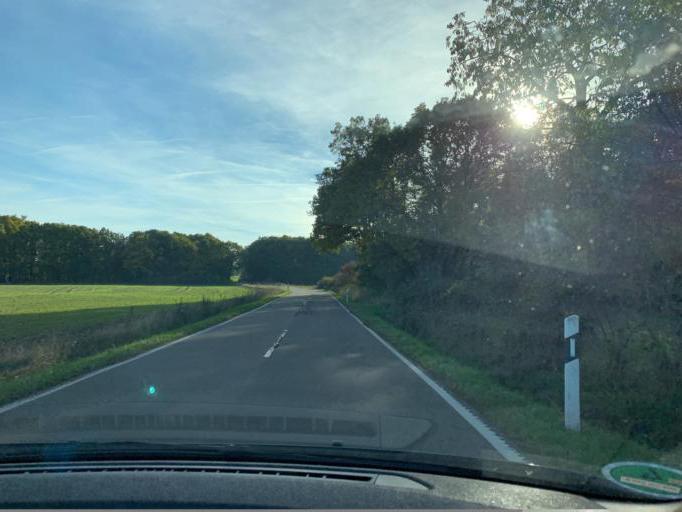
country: DE
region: North Rhine-Westphalia
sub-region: Regierungsbezirk Koln
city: Nideggen
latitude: 50.7147
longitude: 6.5164
